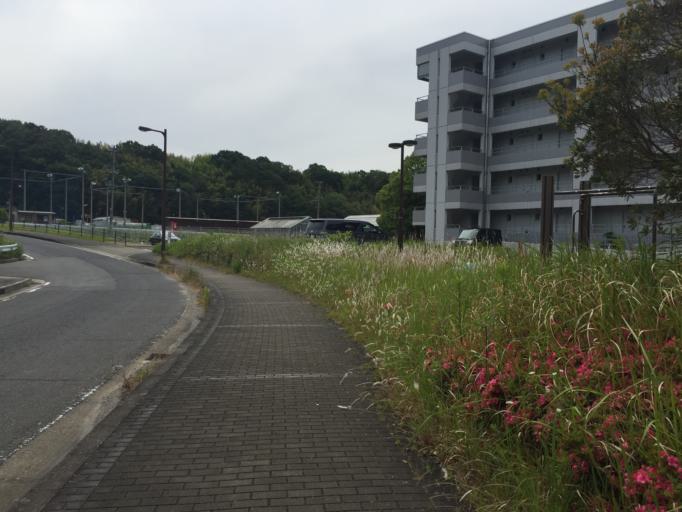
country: JP
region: Nara
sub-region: Ikoma-shi
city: Ikoma
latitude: 34.7349
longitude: 135.7359
